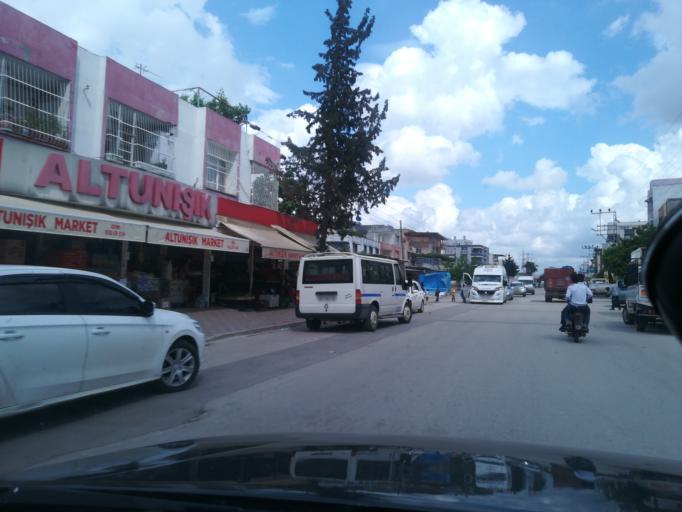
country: TR
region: Adana
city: Yuregir
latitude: 36.9775
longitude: 35.3825
